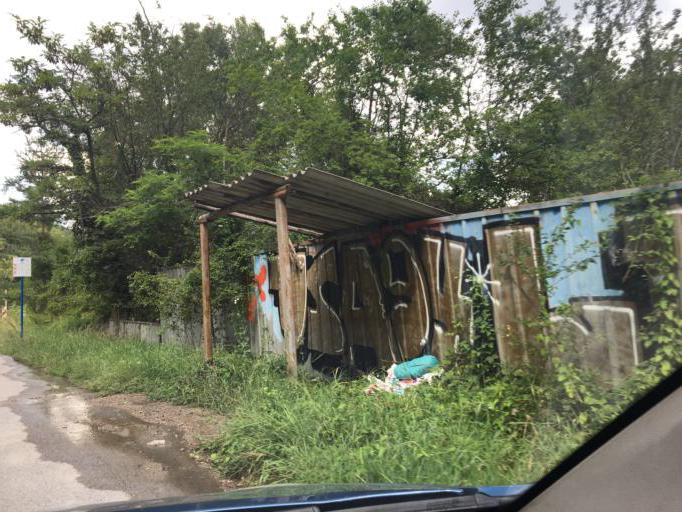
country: BG
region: Sofia-Capital
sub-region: Stolichna Obshtina
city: Sofia
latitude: 42.5952
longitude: 23.3643
